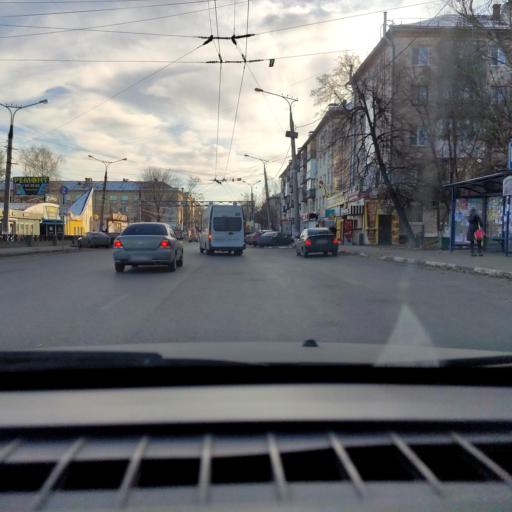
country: RU
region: Samara
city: Tol'yatti
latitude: 53.5095
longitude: 49.4156
